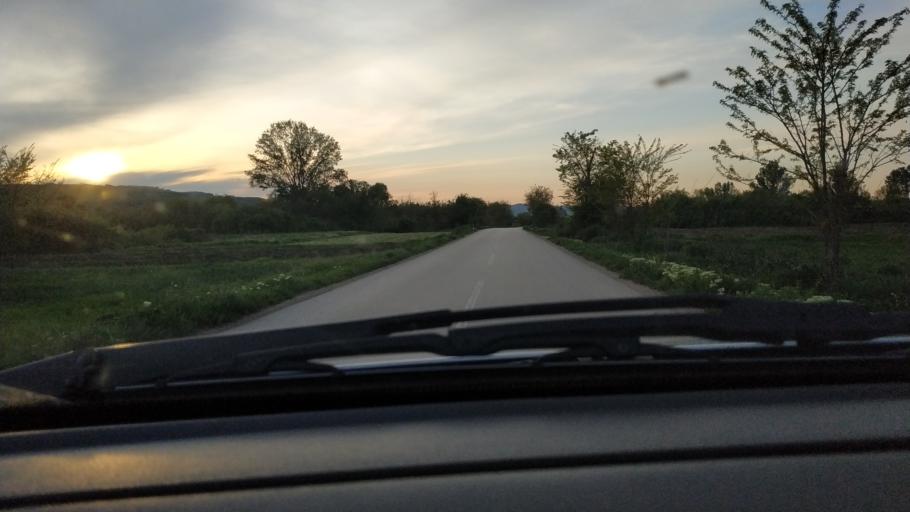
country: RS
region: Central Serbia
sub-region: Nisavski Okrug
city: Aleksinac
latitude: 43.5489
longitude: 21.6204
